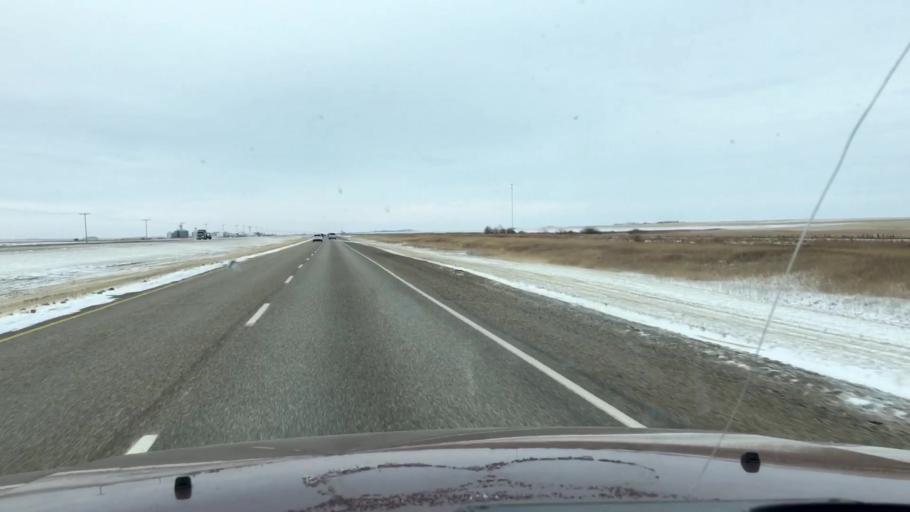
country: CA
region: Saskatchewan
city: Moose Jaw
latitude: 51.0219
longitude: -105.7882
